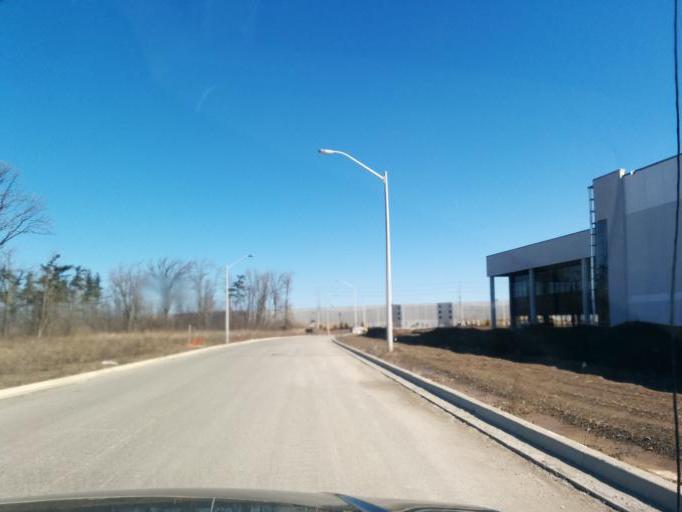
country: CA
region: Ontario
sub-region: Halton
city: Milton
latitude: 43.5283
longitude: -79.9220
